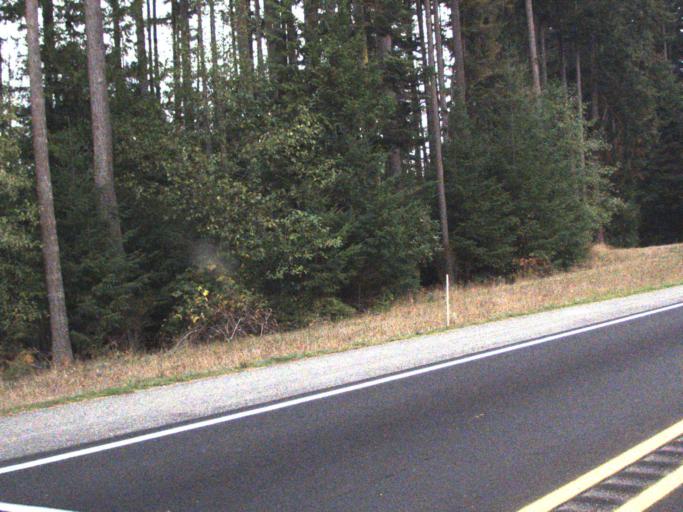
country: US
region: Washington
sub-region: Island County
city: Freeland
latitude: 48.0743
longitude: -122.5676
